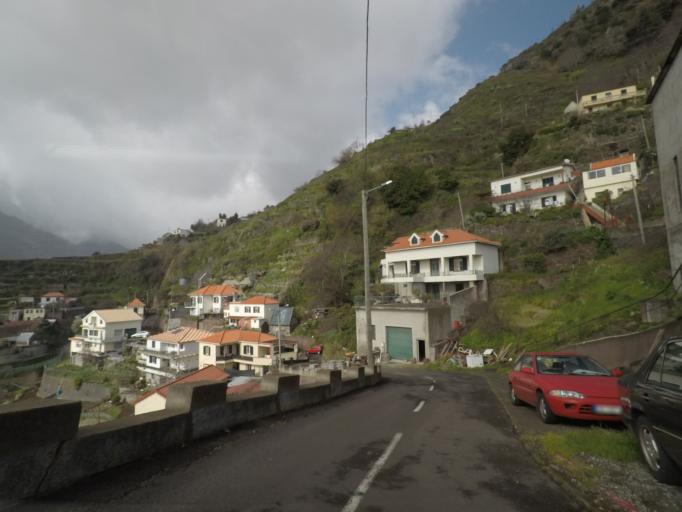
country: PT
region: Madeira
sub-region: Ribeira Brava
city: Campanario
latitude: 32.7060
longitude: -17.0295
